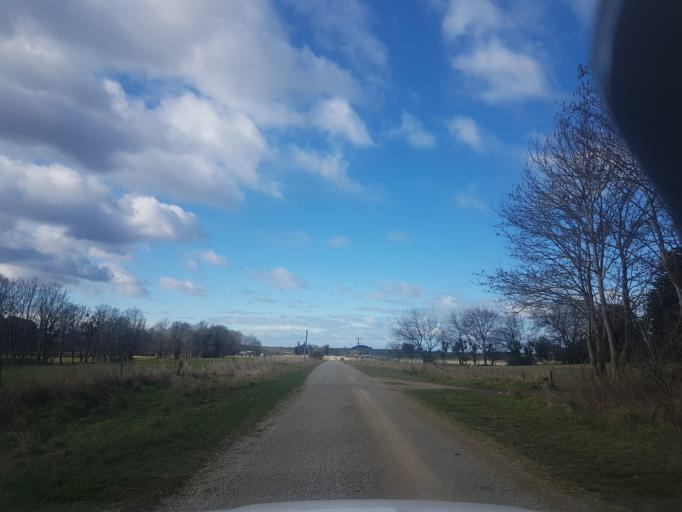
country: NZ
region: Canterbury
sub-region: Timaru District
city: Pleasant Point
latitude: -44.1885
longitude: 171.1756
